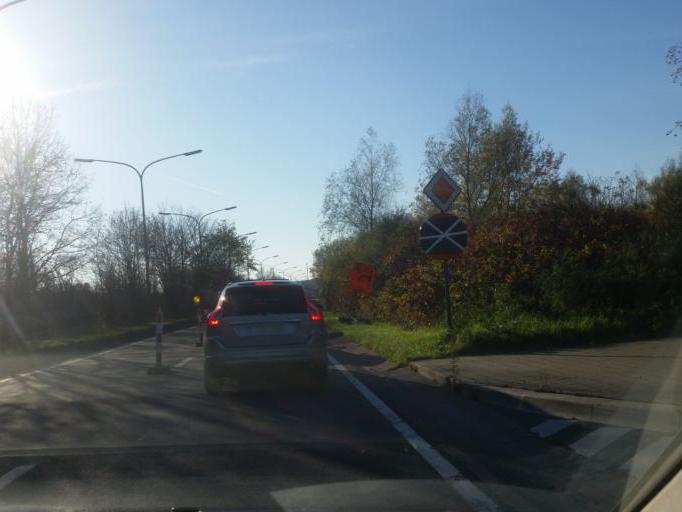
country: BE
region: Flanders
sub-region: Provincie Vlaams-Brabant
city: Kraainem
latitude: 50.8740
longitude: 4.4575
